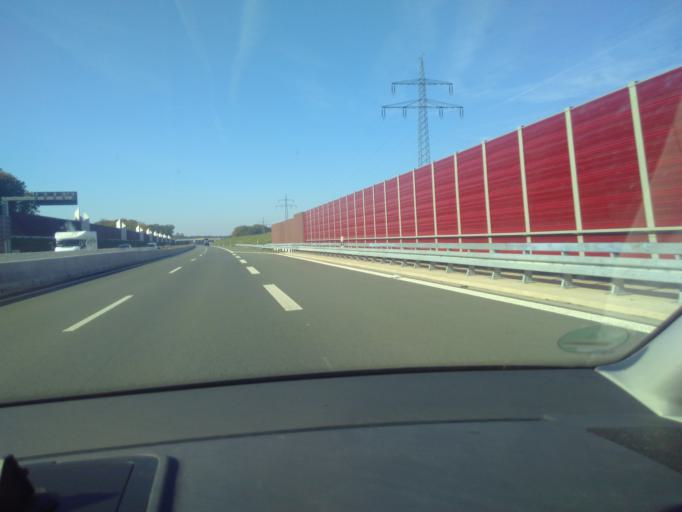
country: DE
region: North Rhine-Westphalia
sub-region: Regierungsbezirk Detmold
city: Steinhagen
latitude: 52.0104
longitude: 8.4243
